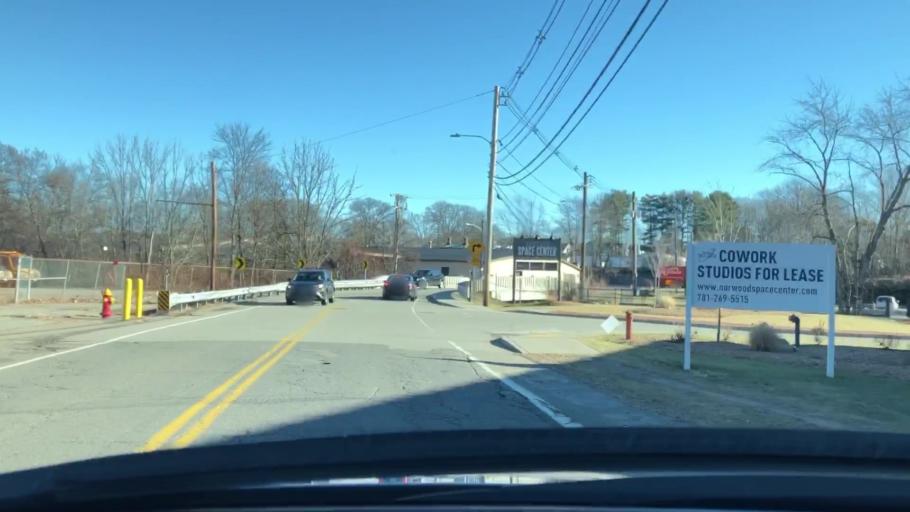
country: US
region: Massachusetts
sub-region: Norfolk County
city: Norwood
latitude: 42.1729
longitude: -71.2056
